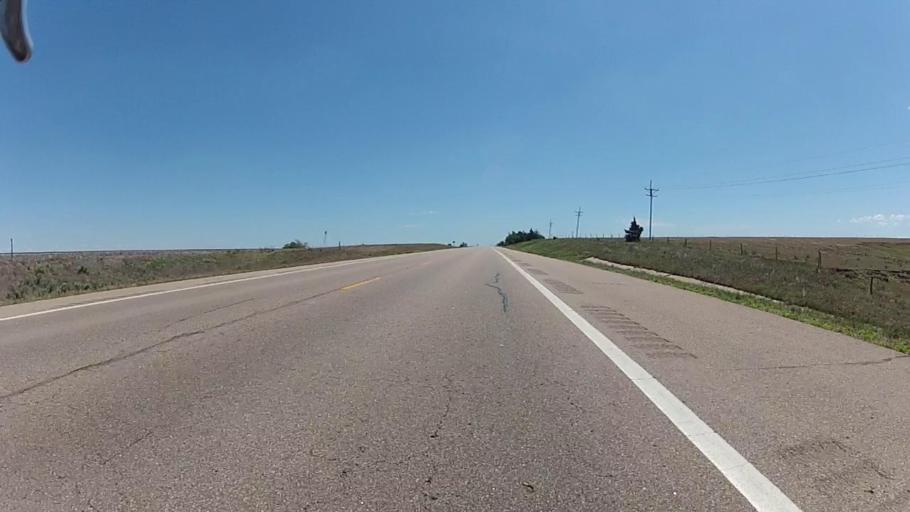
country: US
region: Kansas
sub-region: Ford County
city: Dodge City
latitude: 37.7064
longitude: -100.1333
